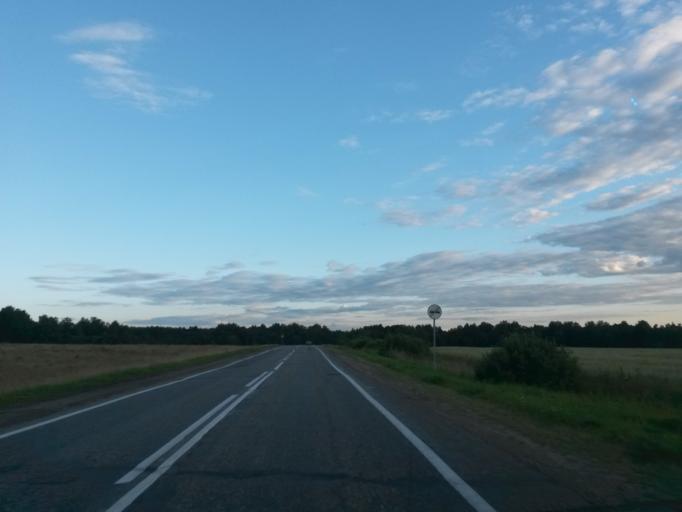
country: RU
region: Jaroslavl
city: Gavrilov-Yam
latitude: 57.4048
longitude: 39.9211
